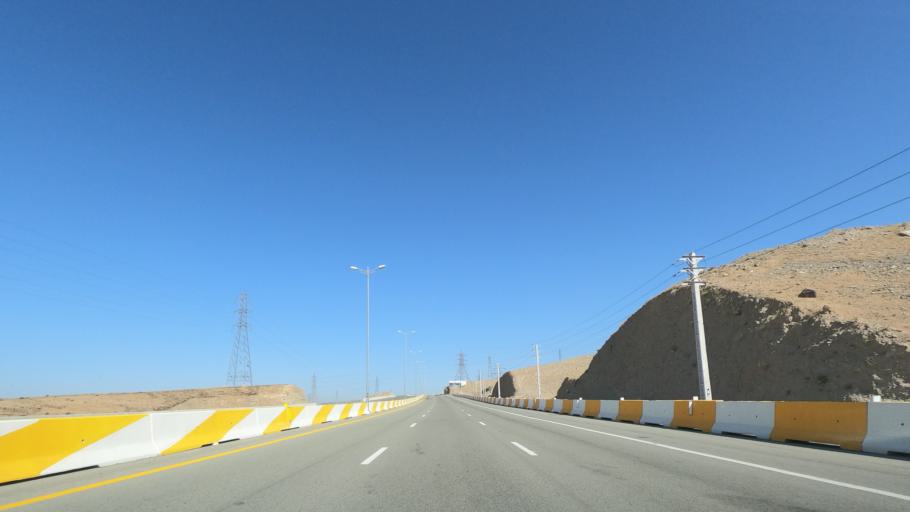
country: IR
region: Tehran
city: Shahr-e Qods
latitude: 35.7721
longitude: 51.0578
